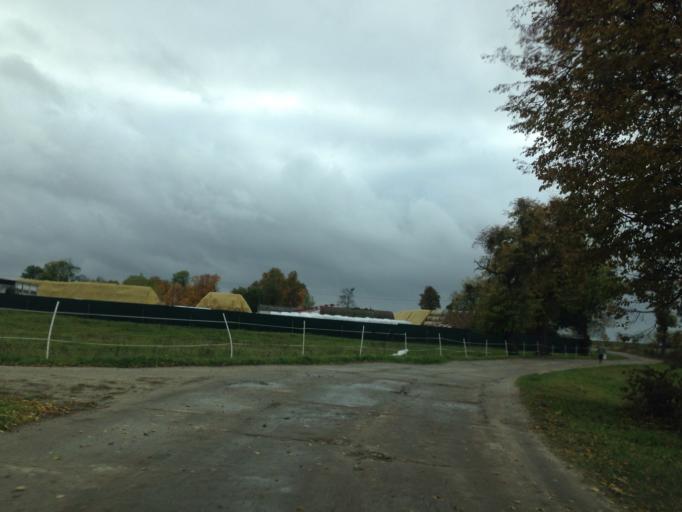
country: PL
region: Pomeranian Voivodeship
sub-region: Powiat kwidzynski
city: Prabuty
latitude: 53.6919
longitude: 19.2570
